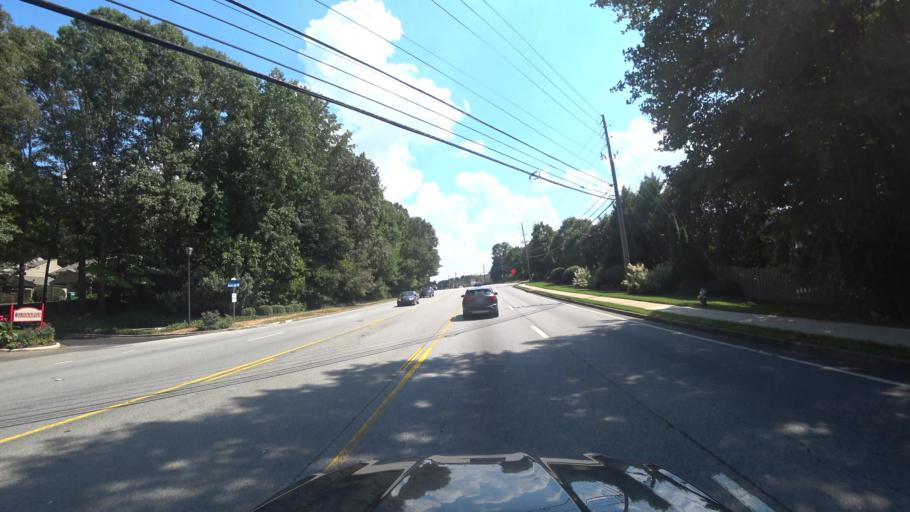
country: US
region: Georgia
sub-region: Gwinnett County
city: Norcross
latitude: 33.9568
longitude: -84.2452
